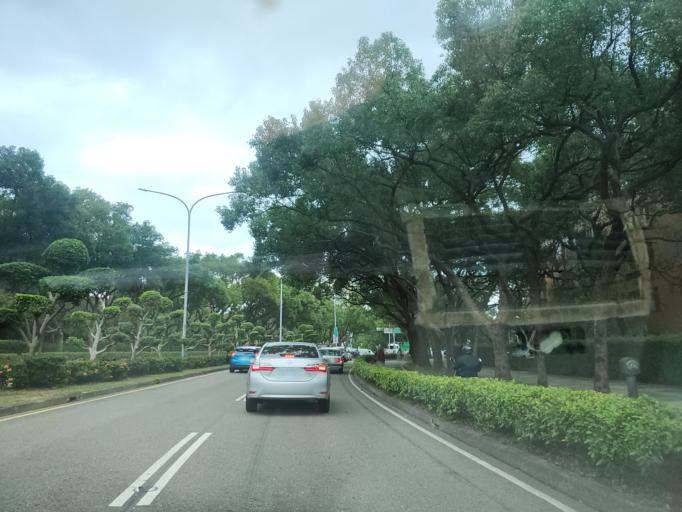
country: TW
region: Taiwan
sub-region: Hsinchu
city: Hsinchu
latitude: 24.7794
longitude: 121.0066
